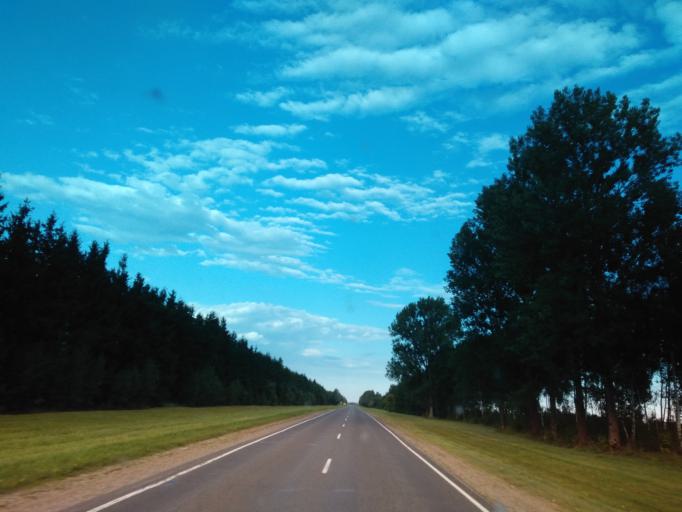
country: BY
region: Minsk
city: Uzda
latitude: 53.4388
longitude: 27.3105
